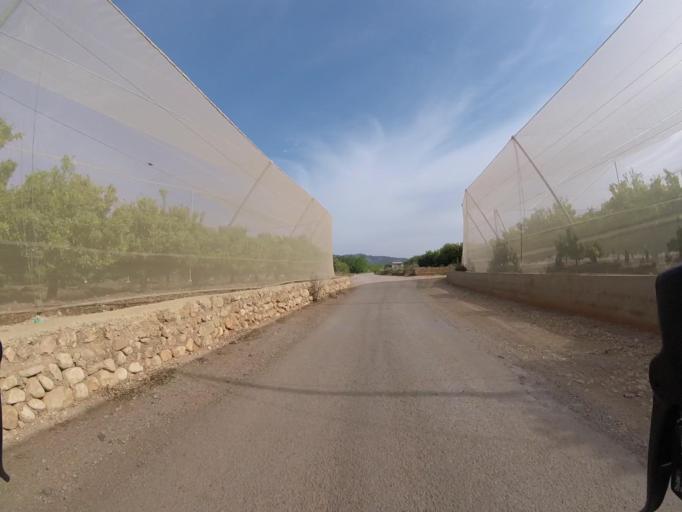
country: ES
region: Valencia
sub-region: Provincia de Castello
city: Alcala de Xivert
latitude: 40.2782
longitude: 0.2584
